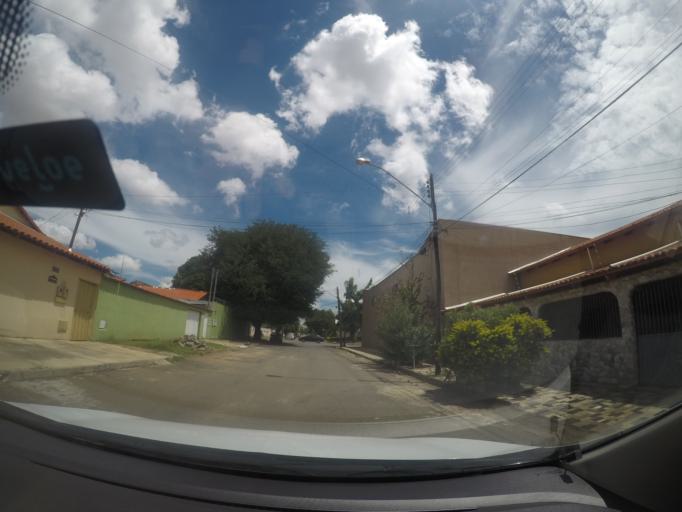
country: BR
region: Goias
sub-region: Goiania
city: Goiania
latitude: -16.6775
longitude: -49.3159
